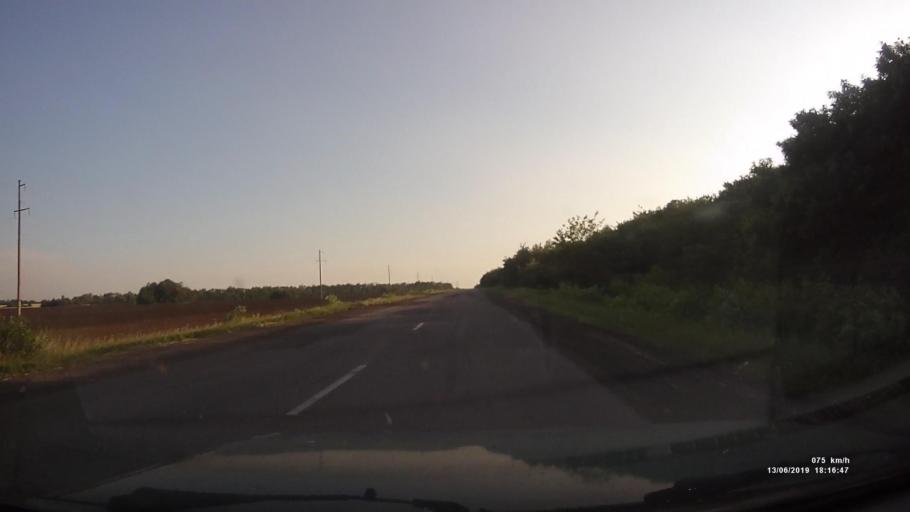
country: RU
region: Rostov
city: Kazanskaya
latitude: 49.9257
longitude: 41.3335
